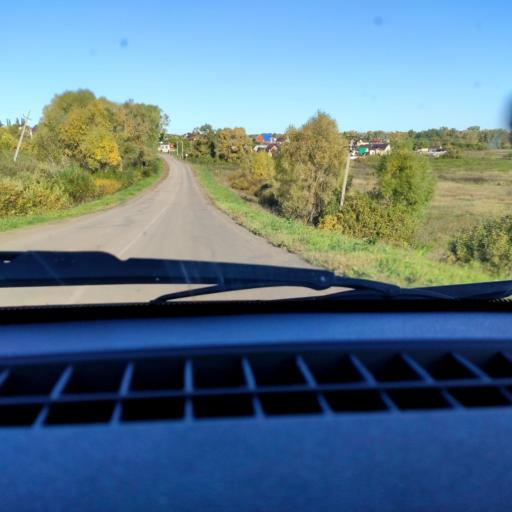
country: RU
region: Bashkortostan
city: Avdon
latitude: 54.6022
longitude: 55.7978
